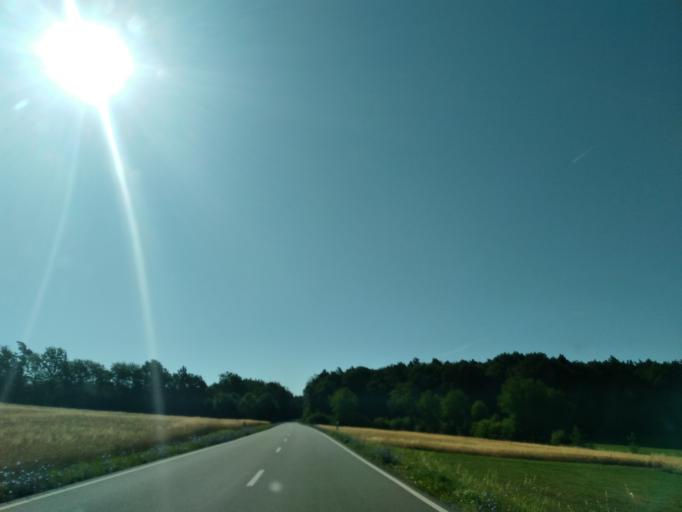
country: DE
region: Baden-Wuerttemberg
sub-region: Karlsruhe Region
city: Mudau
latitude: 49.5111
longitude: 9.2210
